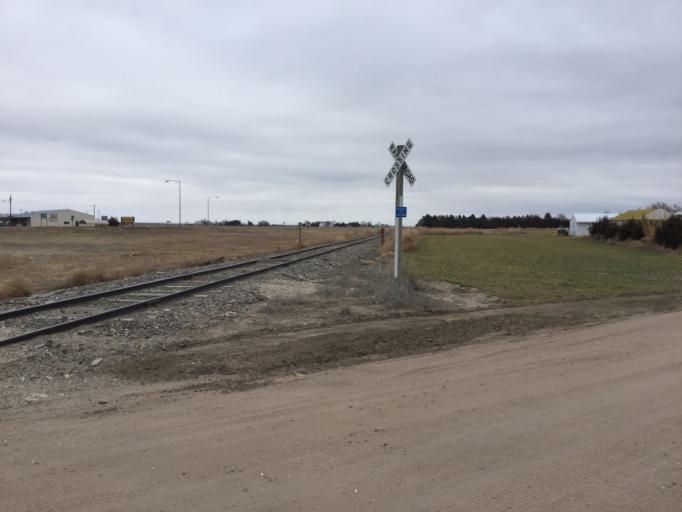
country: US
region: Kansas
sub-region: Pawnee County
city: Larned
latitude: 38.1889
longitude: -99.0833
